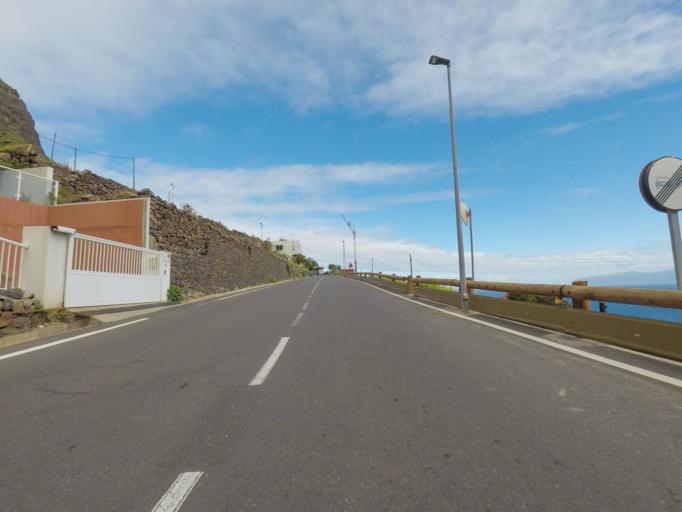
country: ES
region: Canary Islands
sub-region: Provincia de Santa Cruz de Tenerife
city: Hermigua
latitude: 28.1783
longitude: -17.1866
